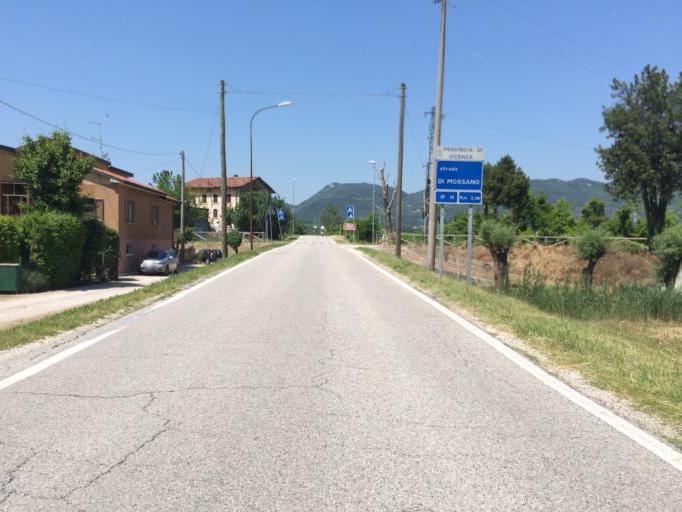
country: IT
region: Veneto
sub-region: Provincia di Vicenza
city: Ponte di Barbarano
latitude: 45.4095
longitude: 11.5829
